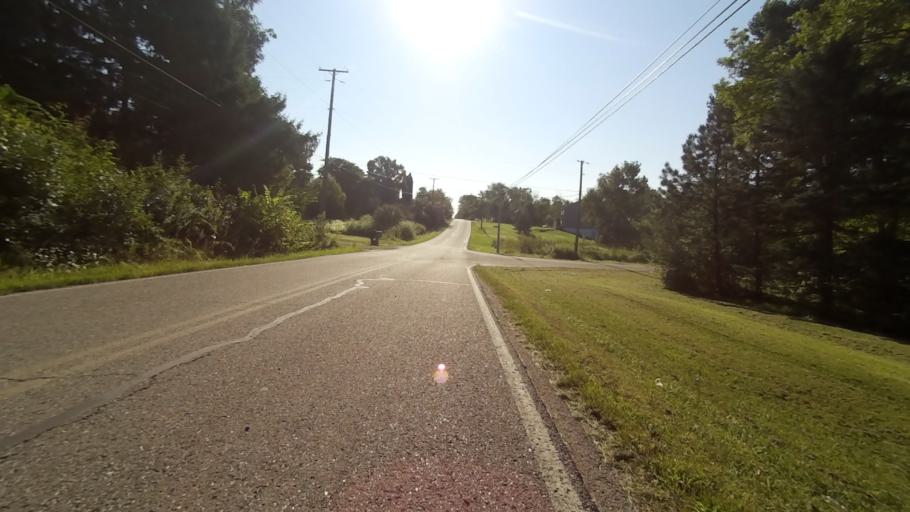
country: US
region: Ohio
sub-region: Portage County
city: Aurora
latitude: 41.2992
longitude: -81.2948
